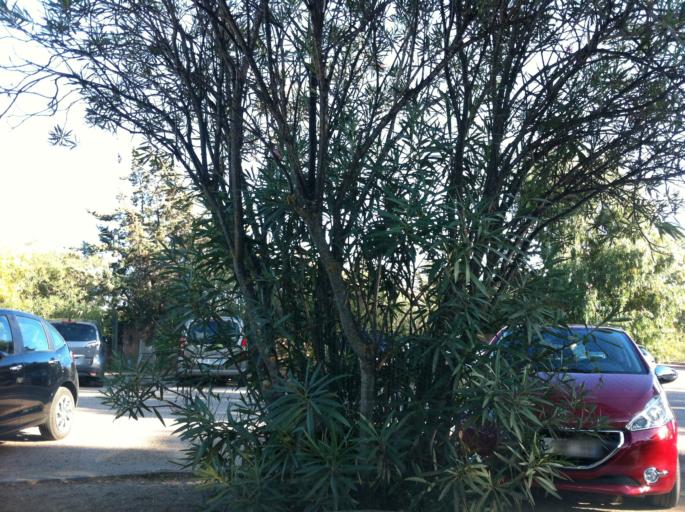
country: FR
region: Corsica
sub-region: Departement de la Corse-du-Sud
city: Porto-Vecchio
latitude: 41.6332
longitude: 9.3449
